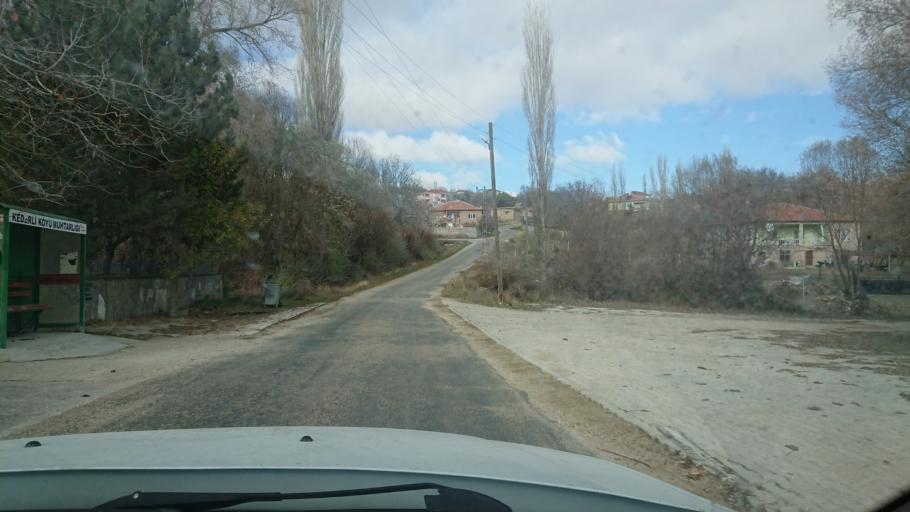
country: TR
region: Aksaray
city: Agacoren
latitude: 38.8203
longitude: 33.9595
